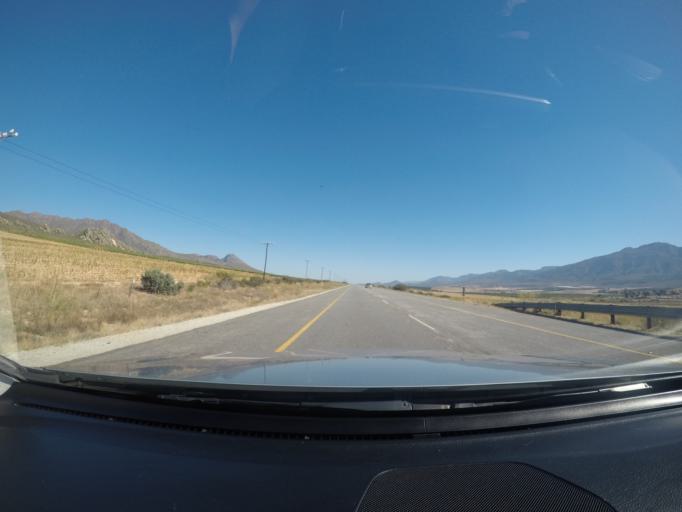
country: ZA
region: Western Cape
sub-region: West Coast District Municipality
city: Piketberg
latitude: -32.5839
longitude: 18.9884
